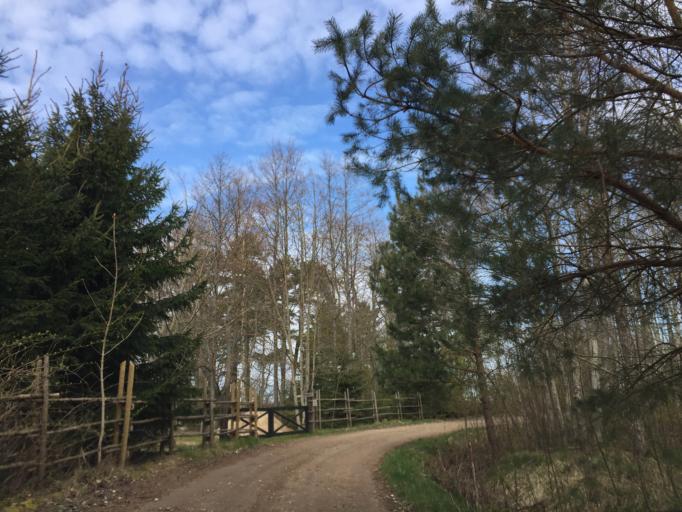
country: LV
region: Salacgrivas
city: Salacgriva
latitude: 57.5430
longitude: 24.3651
